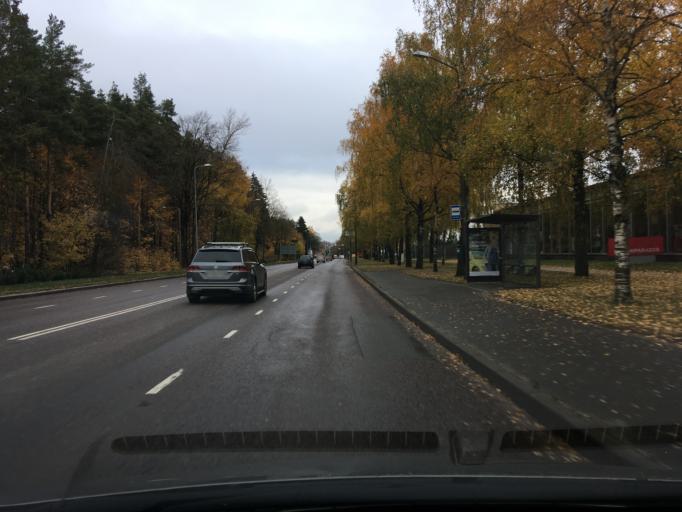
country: EE
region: Tartu
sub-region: Tartu linn
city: Tartu
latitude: 58.3588
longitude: 26.6850
